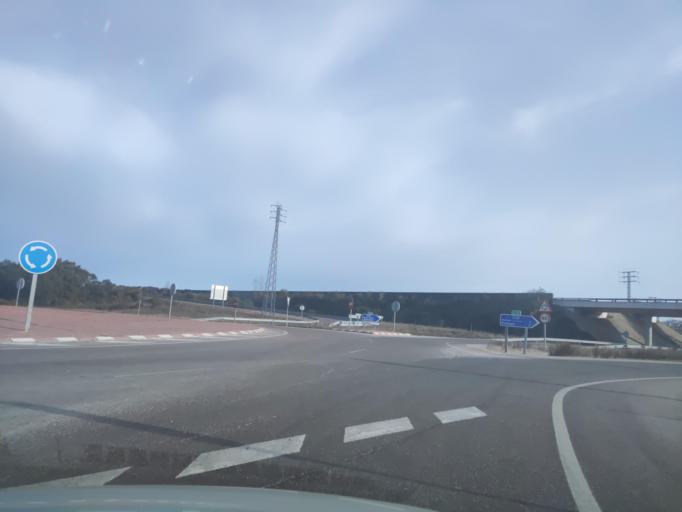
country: ES
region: Castille and Leon
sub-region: Provincia de Salamanca
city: Espeja
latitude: 40.5912
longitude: -6.7055
